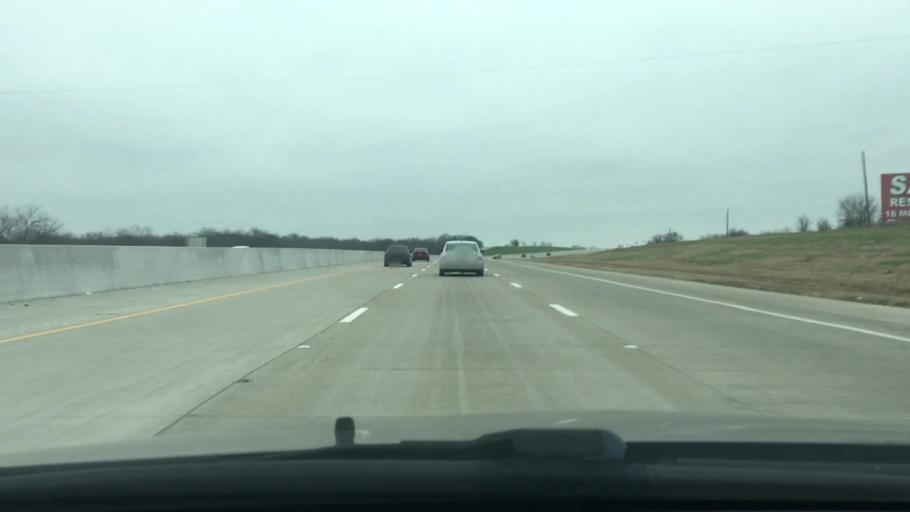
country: US
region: Texas
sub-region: Freestone County
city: Wortham
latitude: 31.8907
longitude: -96.3574
